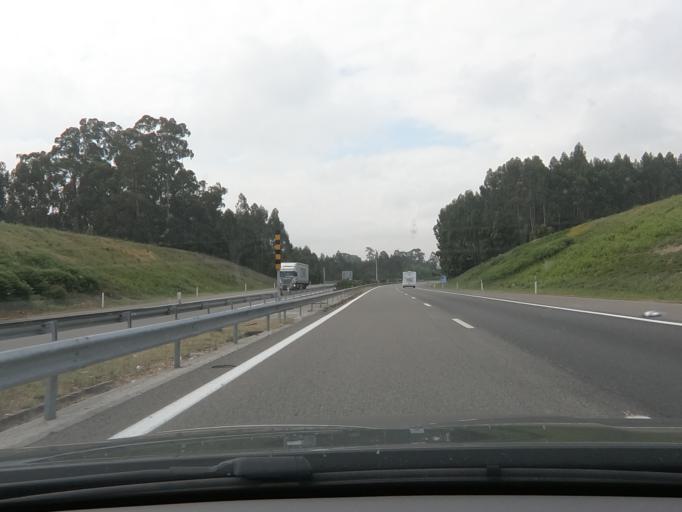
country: PT
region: Aveiro
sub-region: Aveiro
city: Oliveirinha
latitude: 40.5945
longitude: -8.5958
